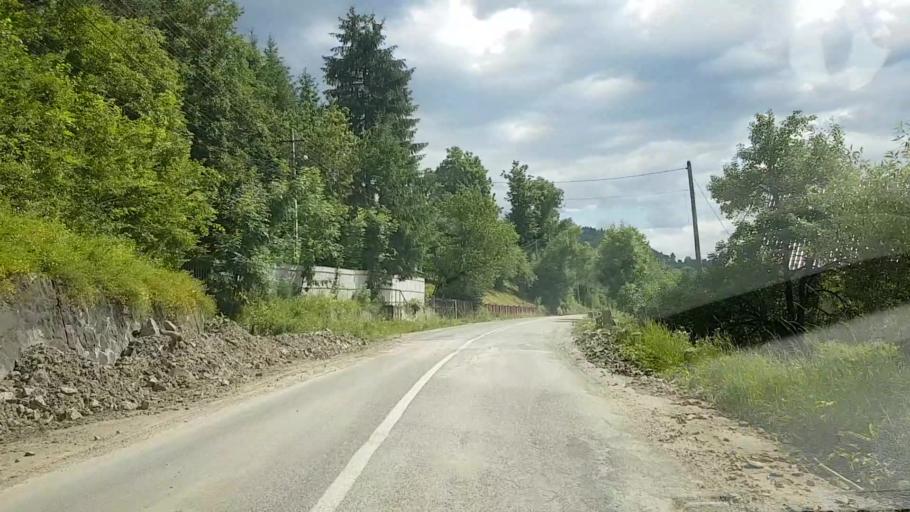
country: RO
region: Neamt
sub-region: Comuna Poiana Teiului
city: Poiana Teiului
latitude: 47.0869
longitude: 25.9706
